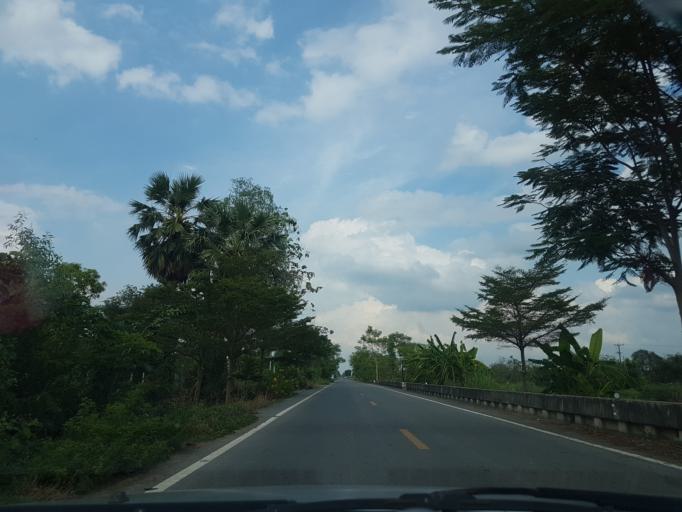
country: TH
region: Pathum Thani
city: Nong Suea
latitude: 14.1996
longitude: 100.8915
